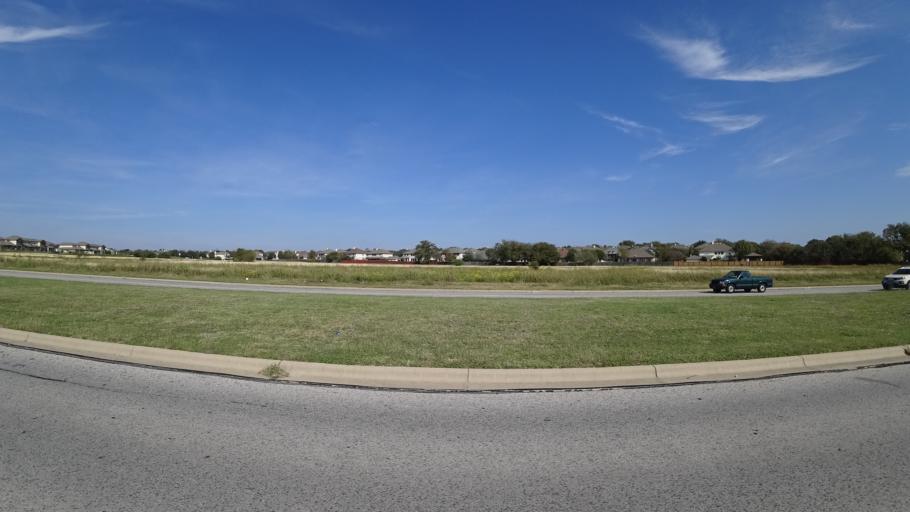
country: US
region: Texas
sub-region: Travis County
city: Pflugerville
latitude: 30.4279
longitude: -97.6329
